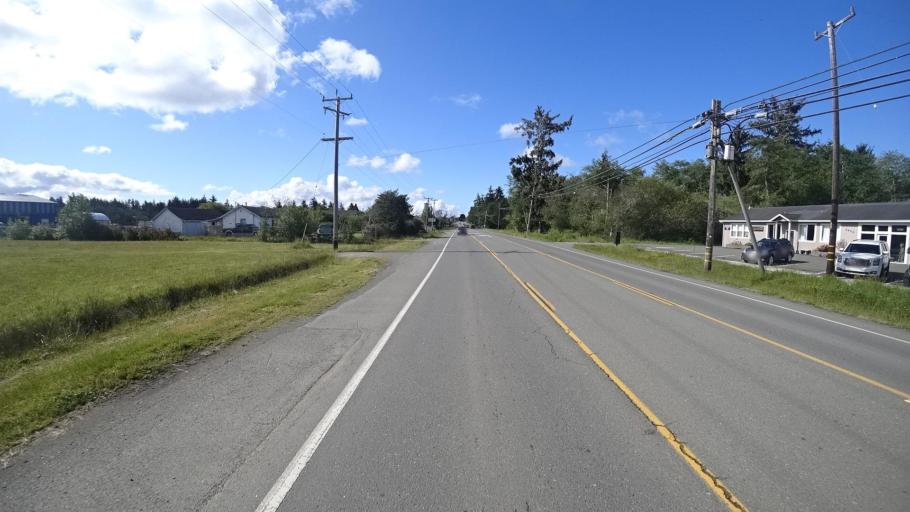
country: US
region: California
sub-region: Humboldt County
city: McKinleyville
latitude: 40.9537
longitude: -124.1008
